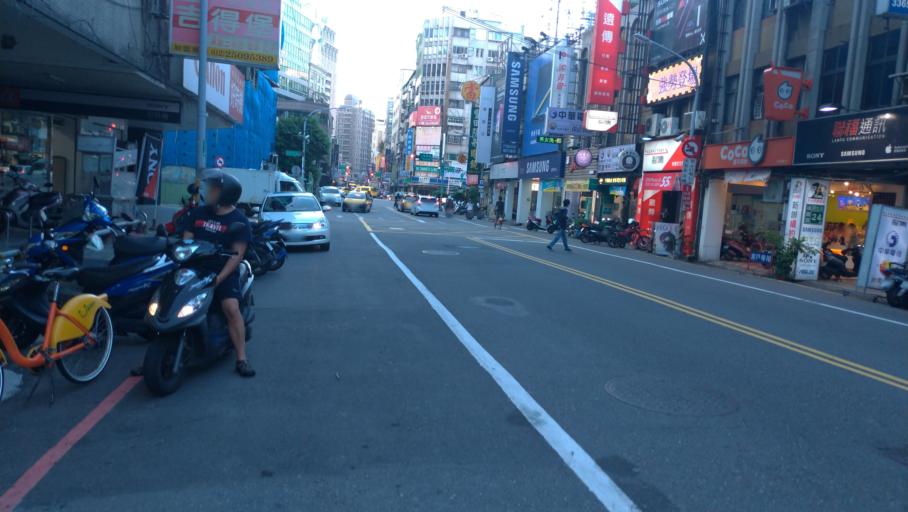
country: TW
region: Taiwan
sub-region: Taoyuan
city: Taoyuan
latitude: 24.9901
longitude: 121.3158
